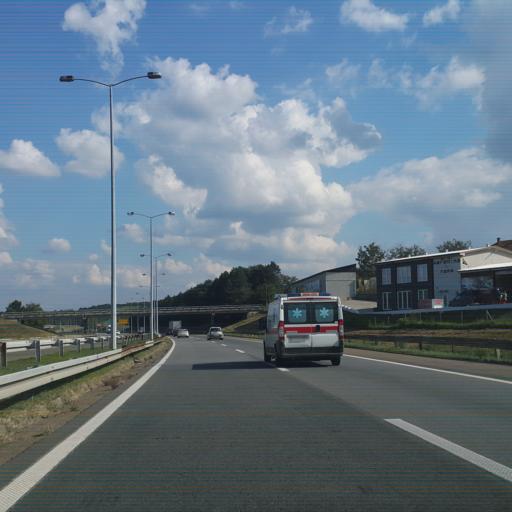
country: RS
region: Central Serbia
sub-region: Belgrade
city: Sopot
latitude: 44.5671
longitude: 20.6576
